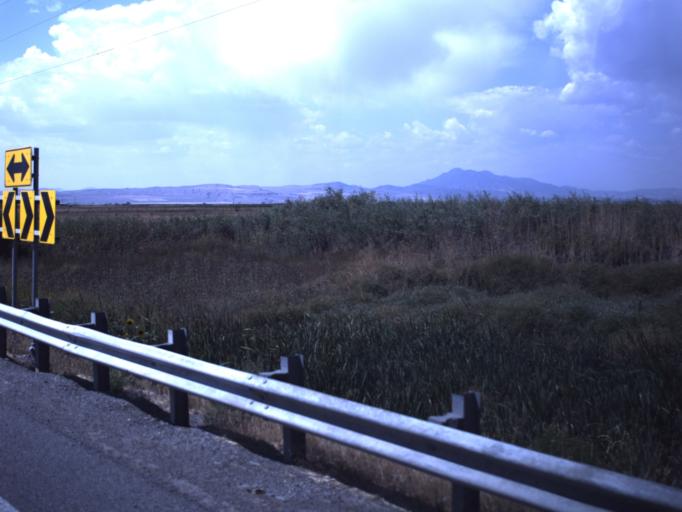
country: US
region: Utah
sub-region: Cache County
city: Logan
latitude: 41.7360
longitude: -111.8794
